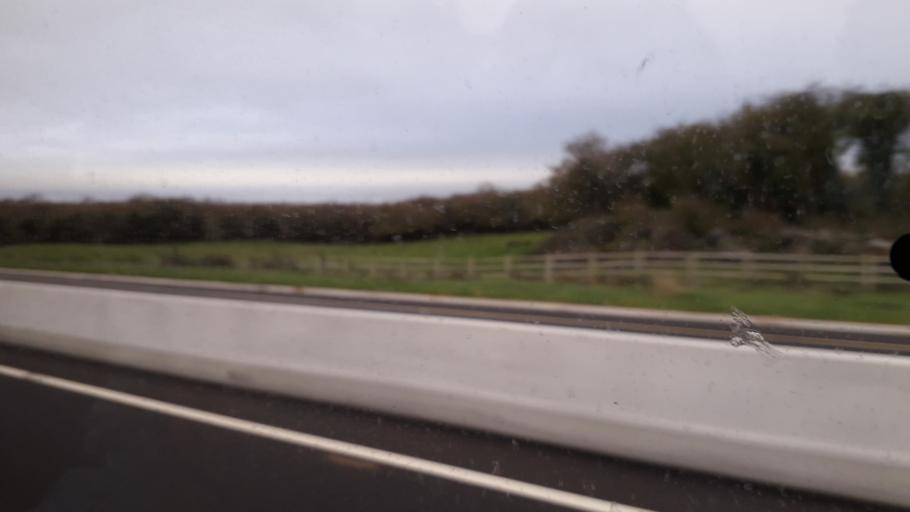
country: IE
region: Connaught
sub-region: County Galway
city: Athenry
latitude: 53.2685
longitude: -8.8101
